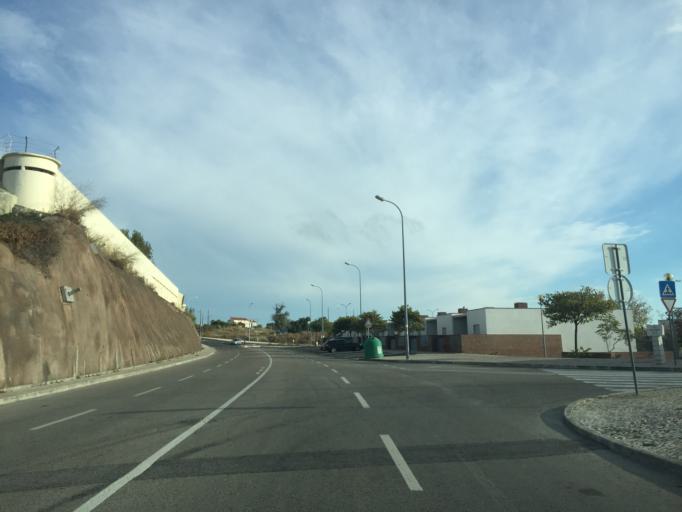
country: PT
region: Lisbon
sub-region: Odivelas
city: Olival do Basto
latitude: 38.7860
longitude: -9.1502
